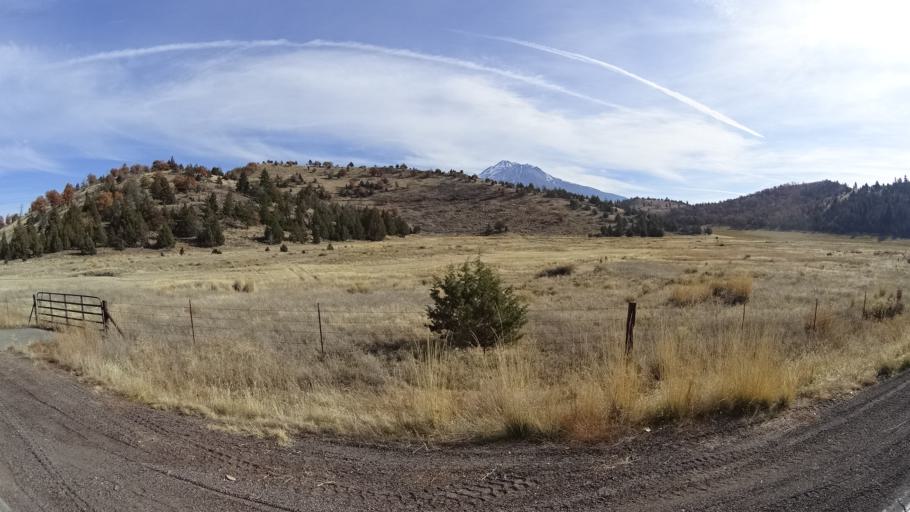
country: US
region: California
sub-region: Siskiyou County
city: Weed
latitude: 41.4855
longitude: -122.4089
